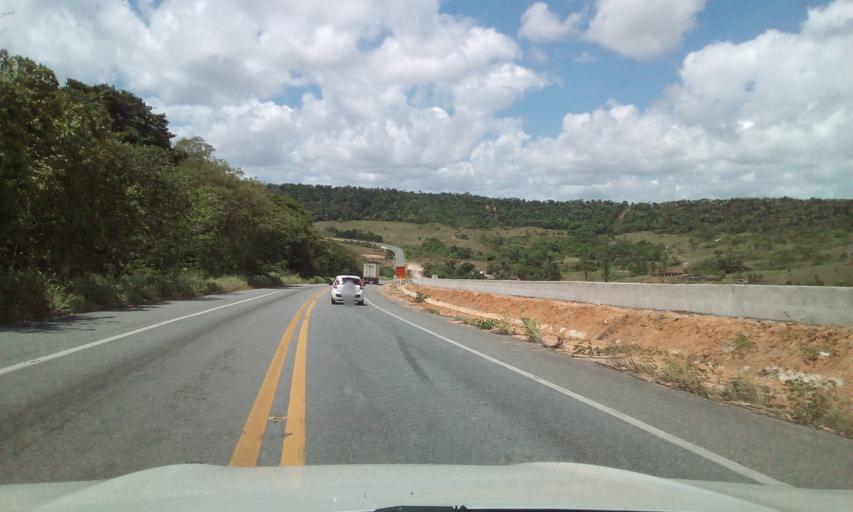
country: BR
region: Alagoas
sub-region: Pilar
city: Pilar
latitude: -9.6500
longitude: -36.0237
